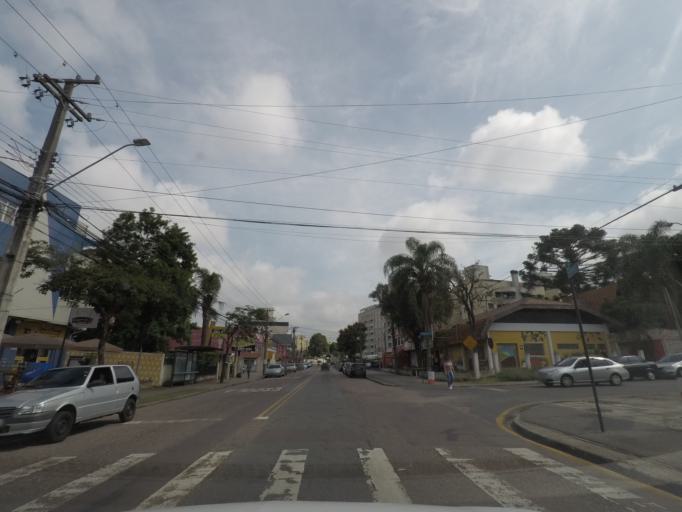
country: BR
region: Parana
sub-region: Curitiba
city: Curitiba
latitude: -25.4751
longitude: -49.2989
